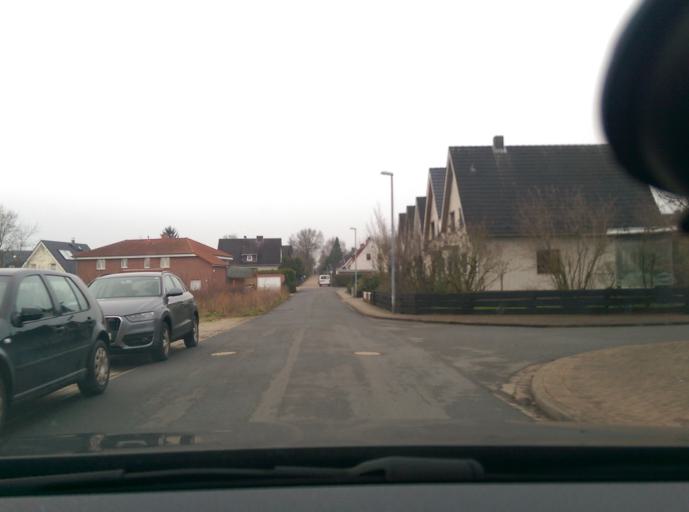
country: DE
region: Lower Saxony
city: Elze
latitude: 52.5441
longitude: 9.7441
